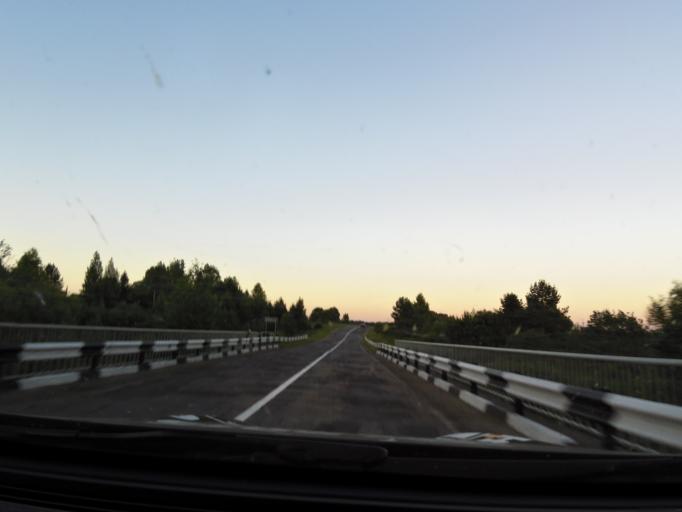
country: RU
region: Jaroslavl
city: Lyubim
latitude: 58.3323
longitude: 40.9008
